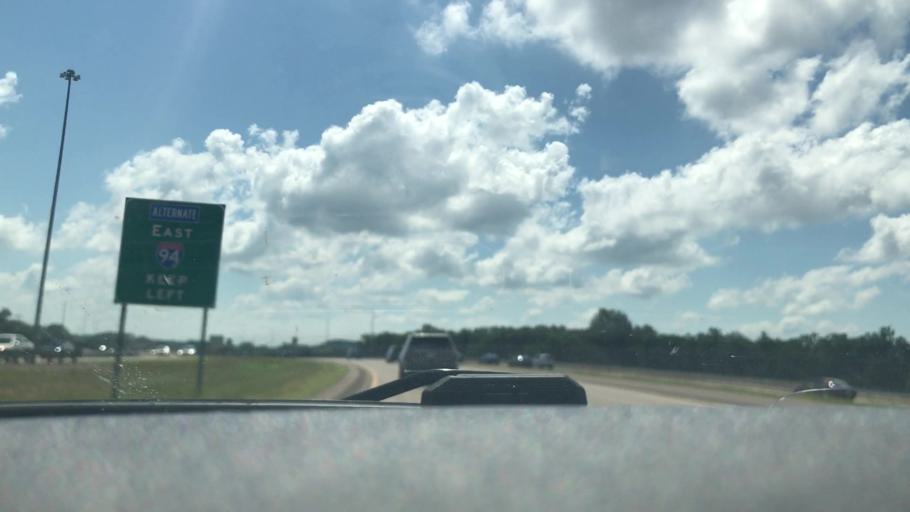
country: US
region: Wisconsin
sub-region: Eau Claire County
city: Altoona
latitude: 44.7860
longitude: -91.4516
